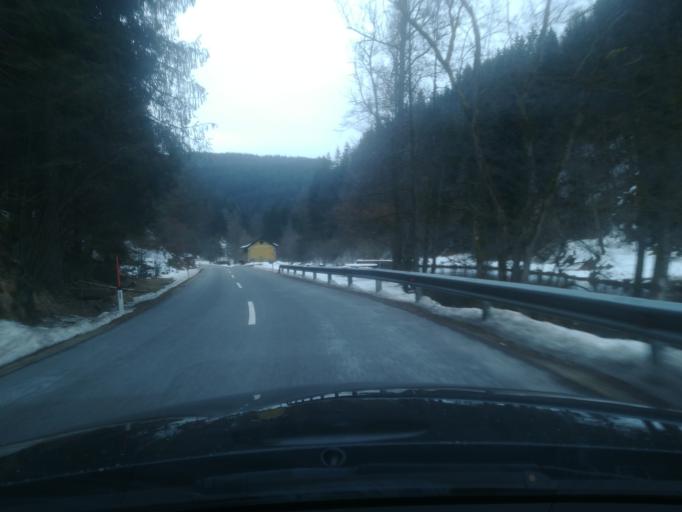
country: AT
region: Upper Austria
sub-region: Politischer Bezirk Perg
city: Perg
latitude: 48.3956
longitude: 14.6389
